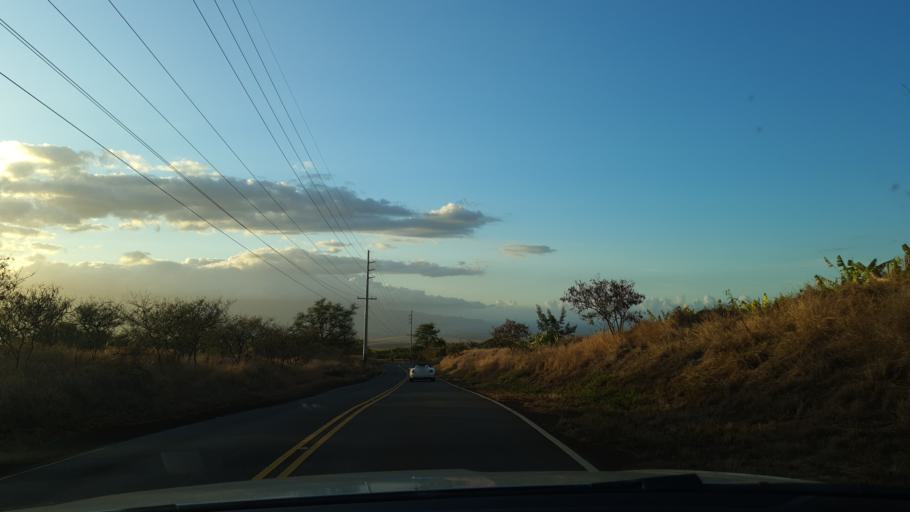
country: US
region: Hawaii
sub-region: Maui County
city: Pukalani
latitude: 20.7928
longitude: -156.3630
